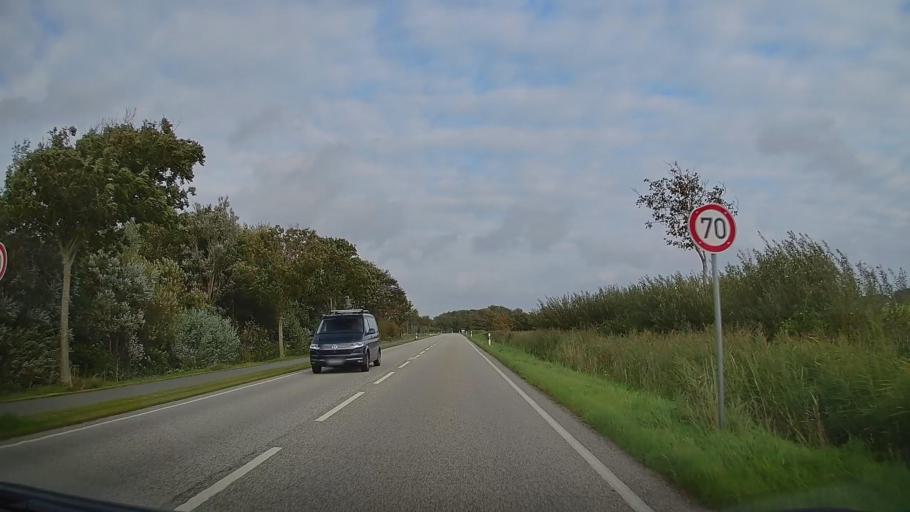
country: DE
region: Schleswig-Holstein
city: Sankt Peter-Ording
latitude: 54.3322
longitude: 8.6210
